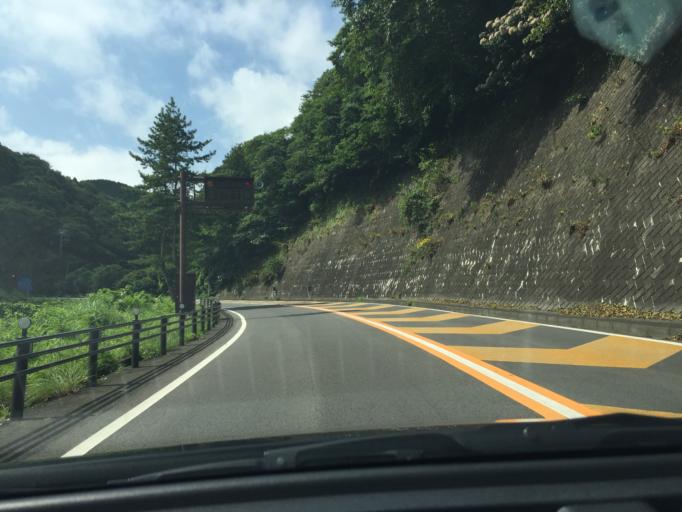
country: JP
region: Shizuoka
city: Ito
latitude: 34.9668
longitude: 139.1232
